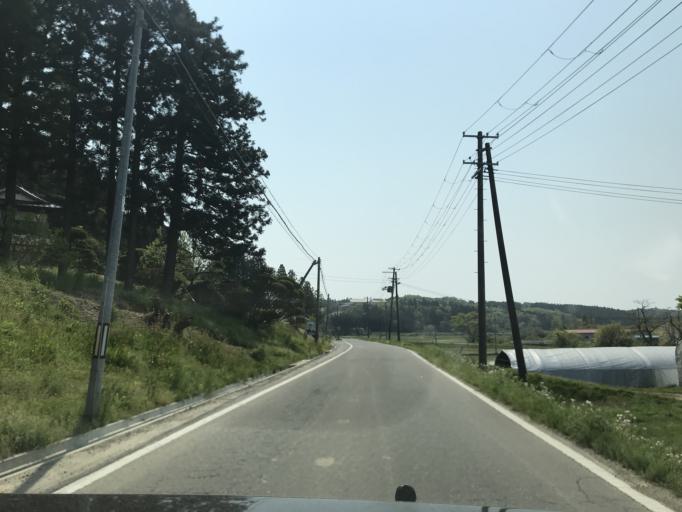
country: JP
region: Iwate
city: Ichinoseki
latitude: 38.8363
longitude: 141.0782
